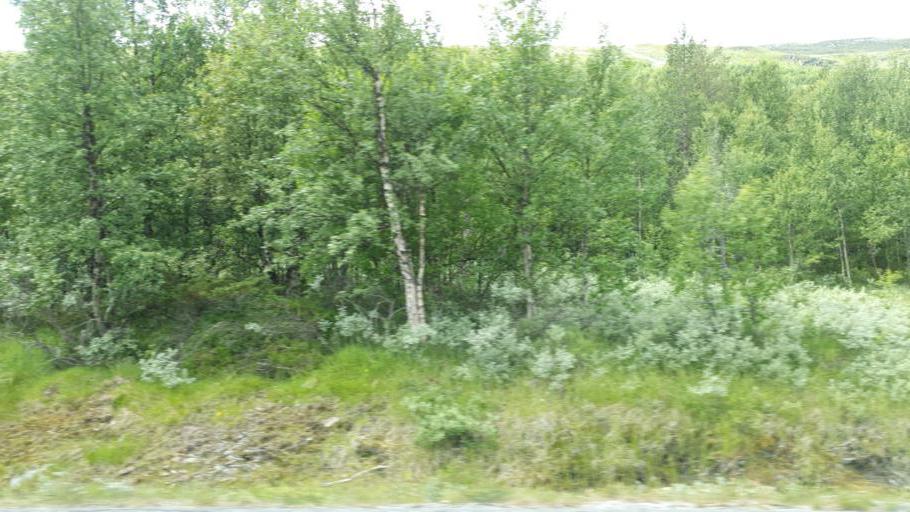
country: NO
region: Oppland
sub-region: Vaga
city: Vagamo
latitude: 61.7528
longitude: 9.0754
